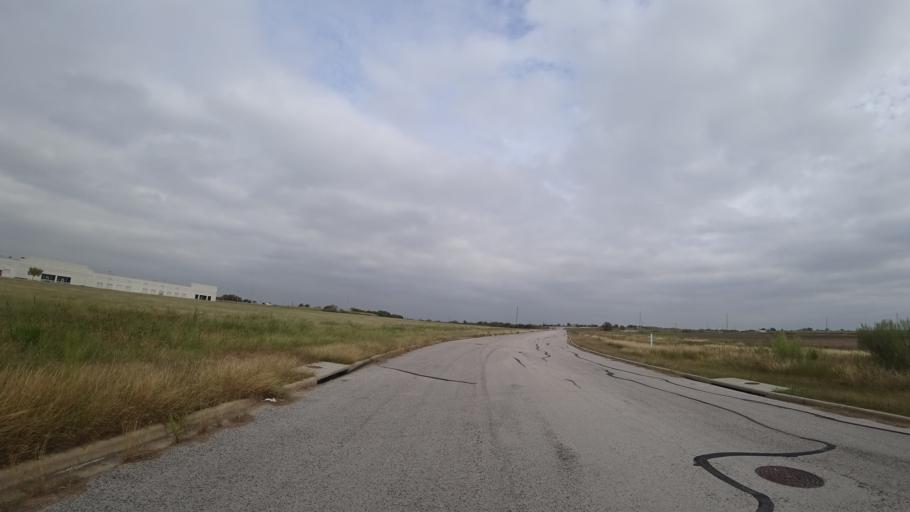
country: US
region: Texas
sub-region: Travis County
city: Manor
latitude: 30.3728
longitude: -97.6073
